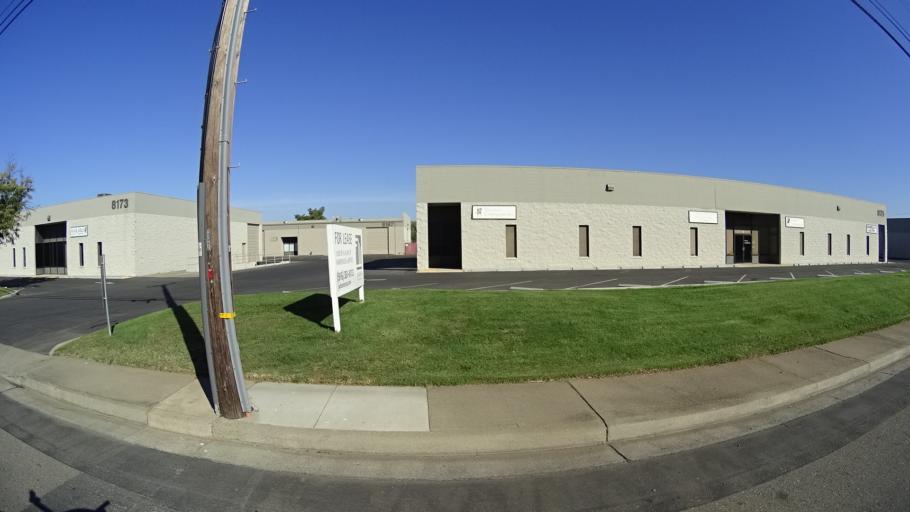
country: US
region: California
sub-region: Sacramento County
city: Florin
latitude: 38.5380
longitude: -121.4058
